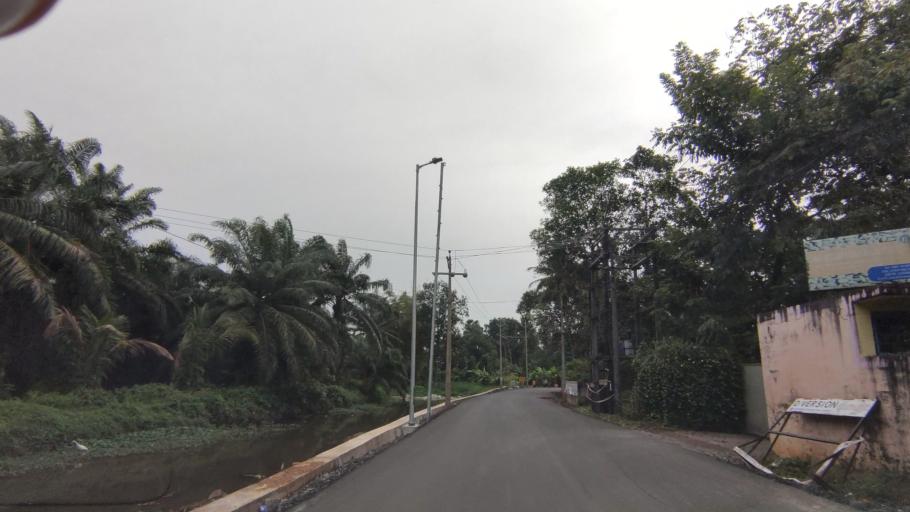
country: IN
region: Kerala
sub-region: Kottayam
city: Kottayam
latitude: 9.6661
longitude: 76.5301
